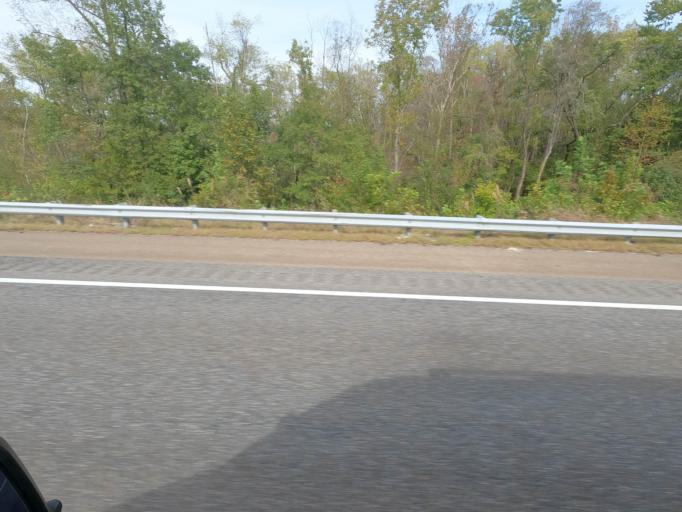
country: US
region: Tennessee
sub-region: Henderson County
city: Lexington
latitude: 35.8012
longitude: -88.3436
